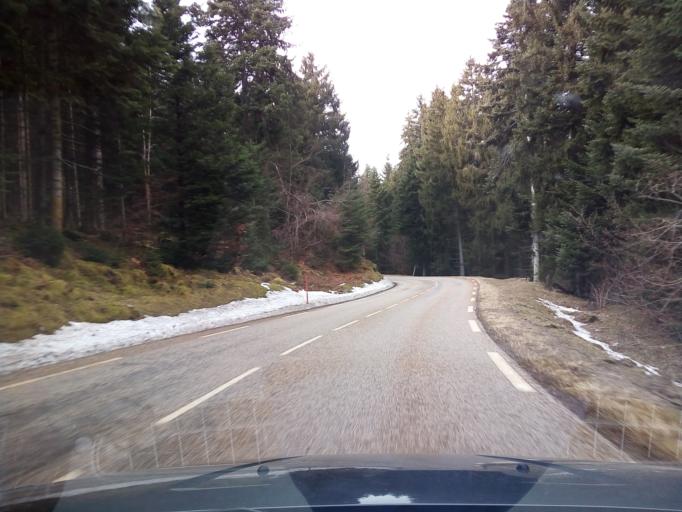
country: FR
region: Rhone-Alpes
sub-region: Departement de l'Isere
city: Revel
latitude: 45.1540
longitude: 5.8745
